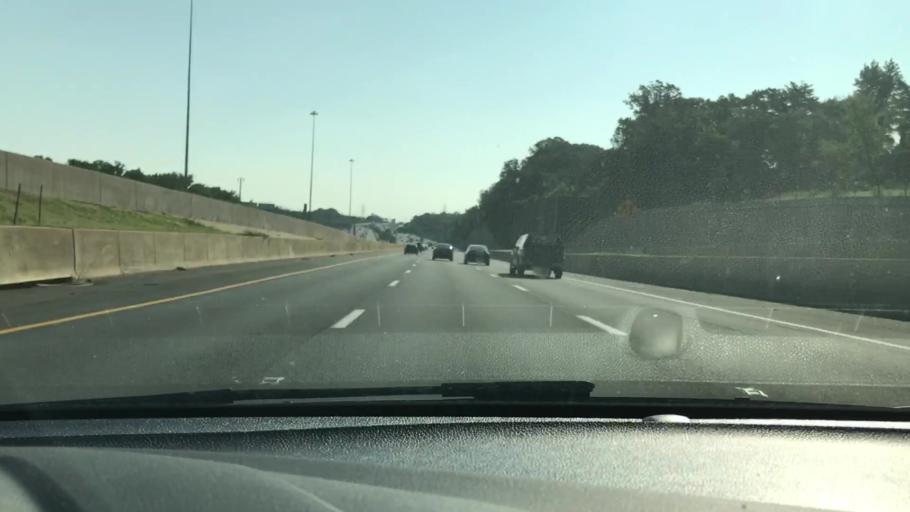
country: US
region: Virginia
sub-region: Fairfax County
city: Springfield
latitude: 38.7900
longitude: -77.1679
